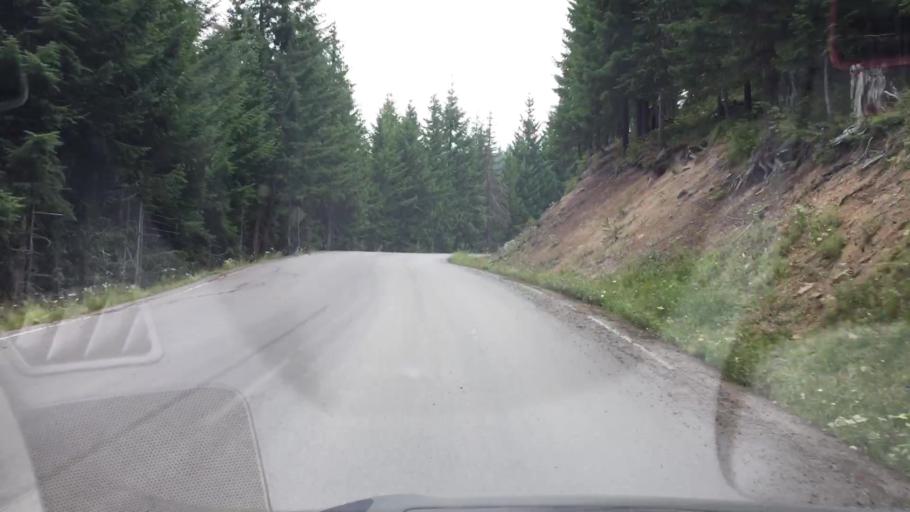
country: US
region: Washington
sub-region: Klickitat County
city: White Salmon
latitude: 46.2089
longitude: -121.6349
